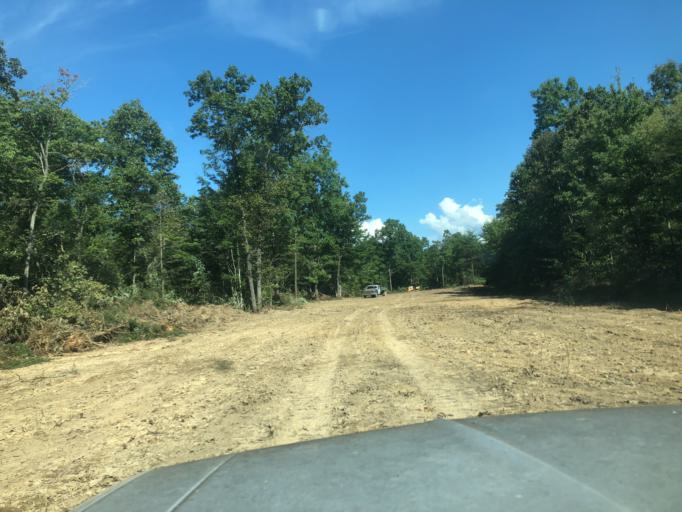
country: US
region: Tennessee
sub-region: Fentress County
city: Jamestown
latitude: 36.3197
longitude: -84.8515
